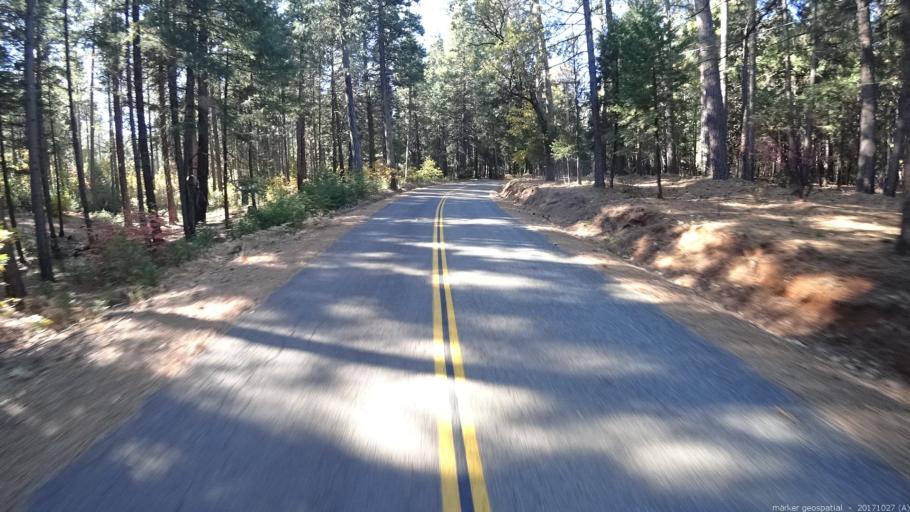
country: US
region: California
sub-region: Shasta County
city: Burney
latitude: 40.8204
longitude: -121.9610
